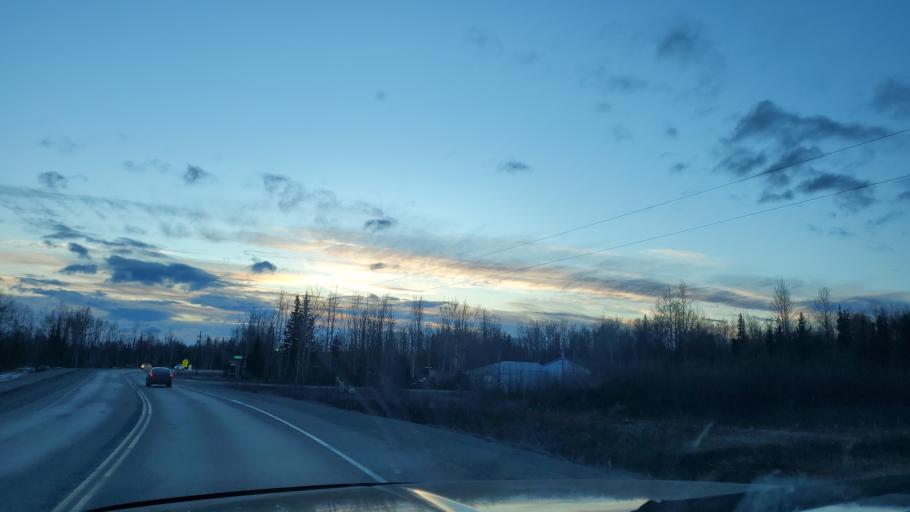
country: US
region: Alaska
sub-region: Matanuska-Susitna Borough
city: Wasilla
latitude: 61.5930
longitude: -149.4383
